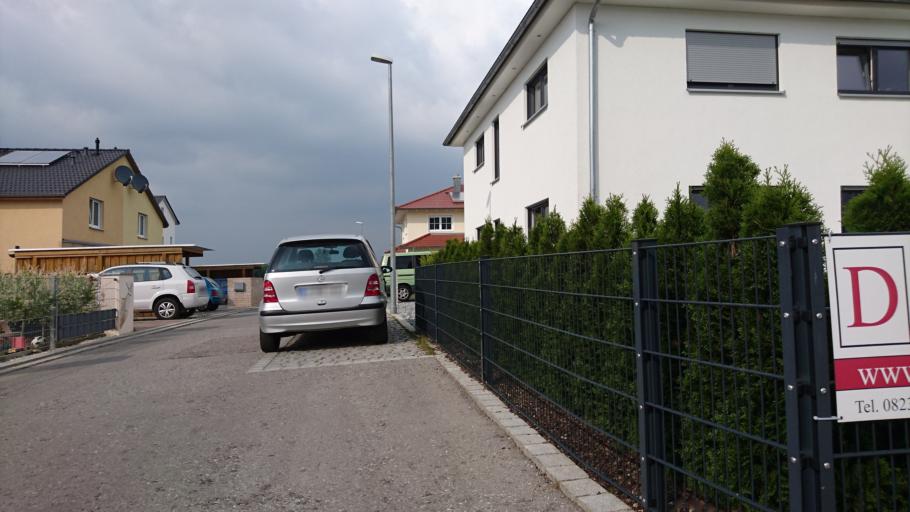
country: DE
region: Bavaria
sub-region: Swabia
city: Diedorf
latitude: 48.3587
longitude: 10.7872
